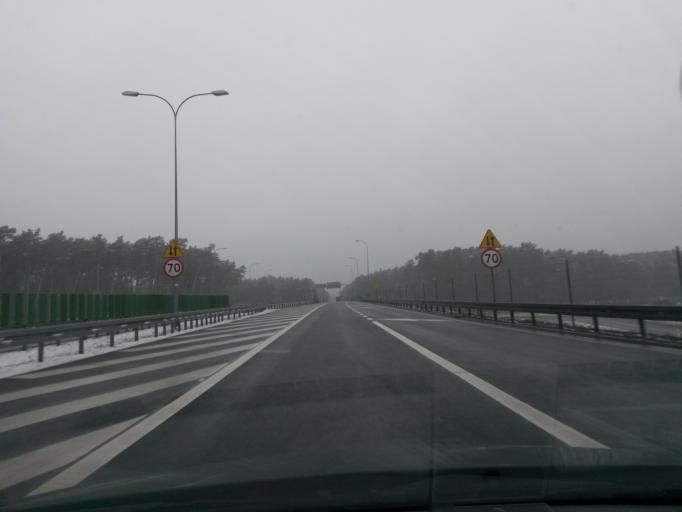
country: PL
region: Kujawsko-Pomorskie
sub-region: Powiat bydgoski
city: Biale Blota
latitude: 53.0985
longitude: 17.8933
